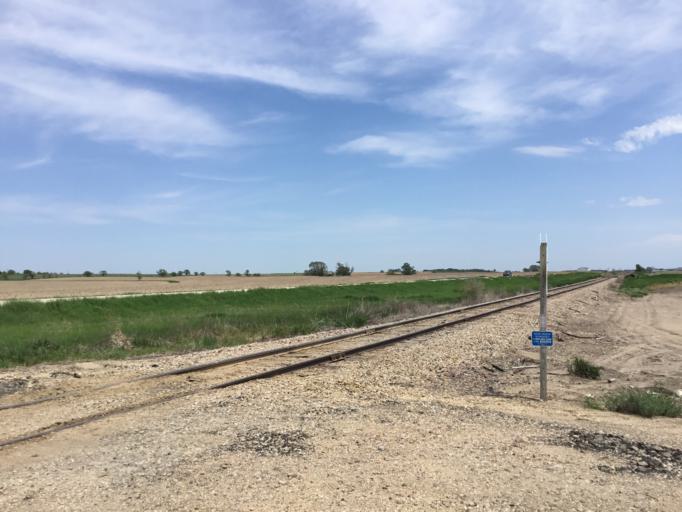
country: US
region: Kansas
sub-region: Mitchell County
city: Beloit
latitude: 39.4902
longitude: -98.2645
